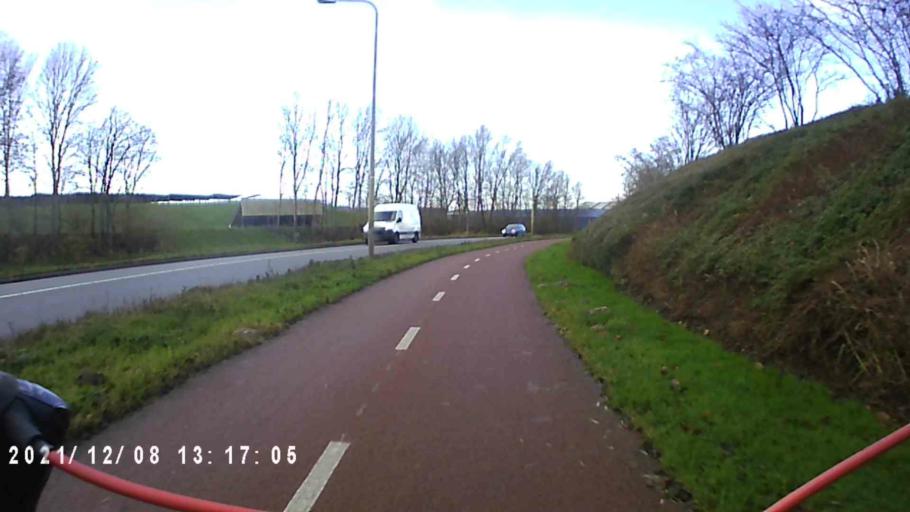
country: NL
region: Groningen
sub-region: Gemeente Haren
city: Haren
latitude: 53.1970
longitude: 6.6174
